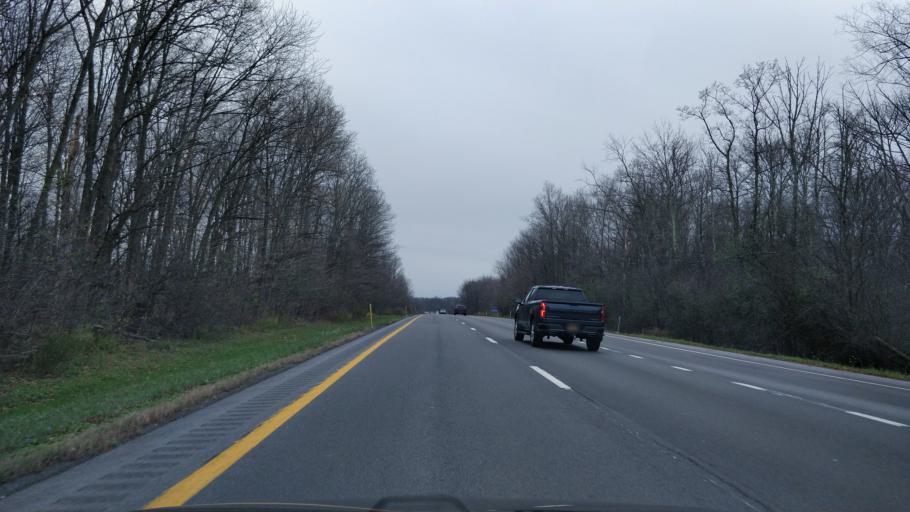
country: US
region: New York
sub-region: Jefferson County
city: Adams
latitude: 43.7358
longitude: -76.0750
